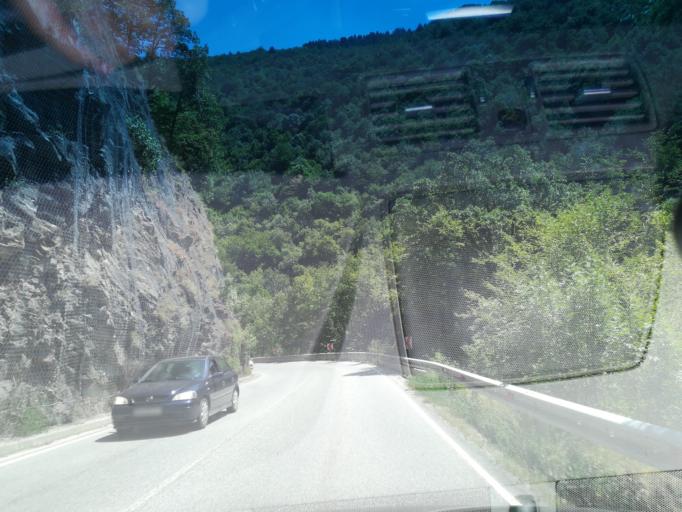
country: BG
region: Plovdiv
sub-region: Obshtina Luki
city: Luki
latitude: 41.9196
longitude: 24.8244
